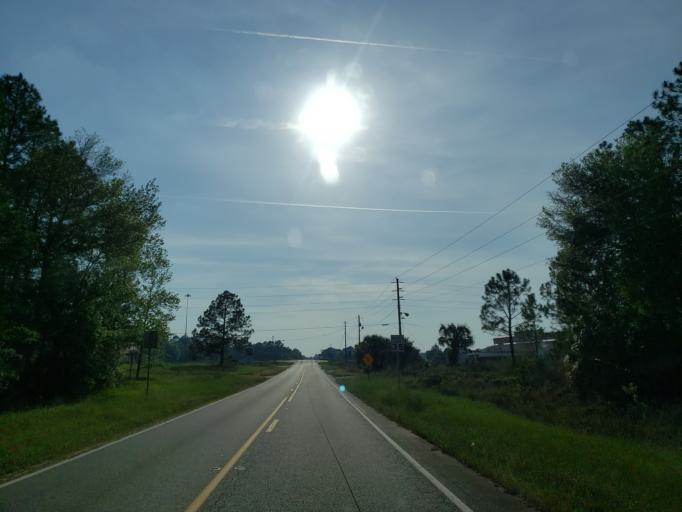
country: US
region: Georgia
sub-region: Tift County
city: Tifton
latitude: 31.5506
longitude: -83.5316
